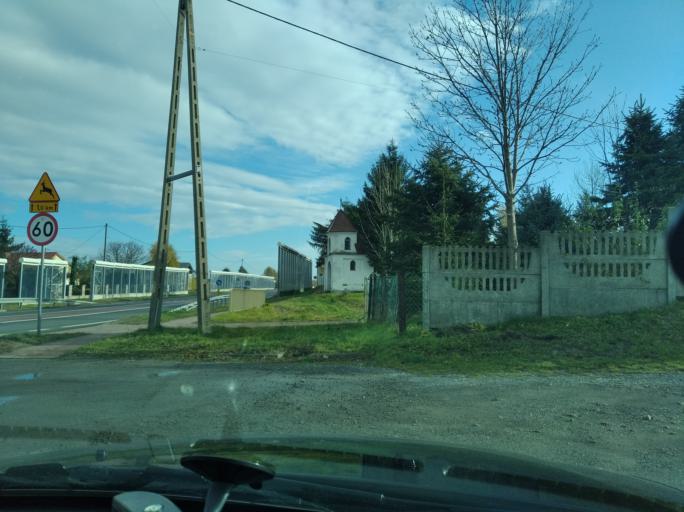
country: PL
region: Subcarpathian Voivodeship
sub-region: Powiat debicki
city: Brzeznica
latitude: 50.0624
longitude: 21.5146
